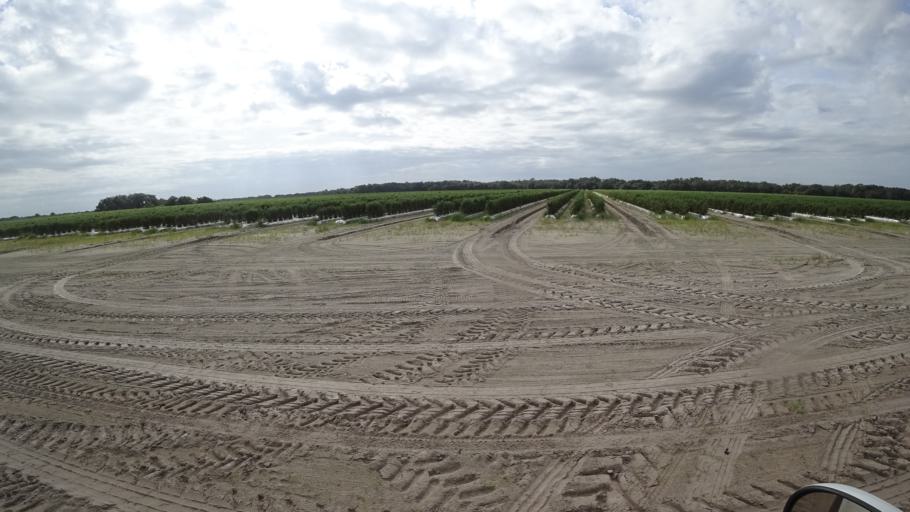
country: US
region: Florida
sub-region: Hillsborough County
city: Wimauma
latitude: 27.5831
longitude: -82.3172
